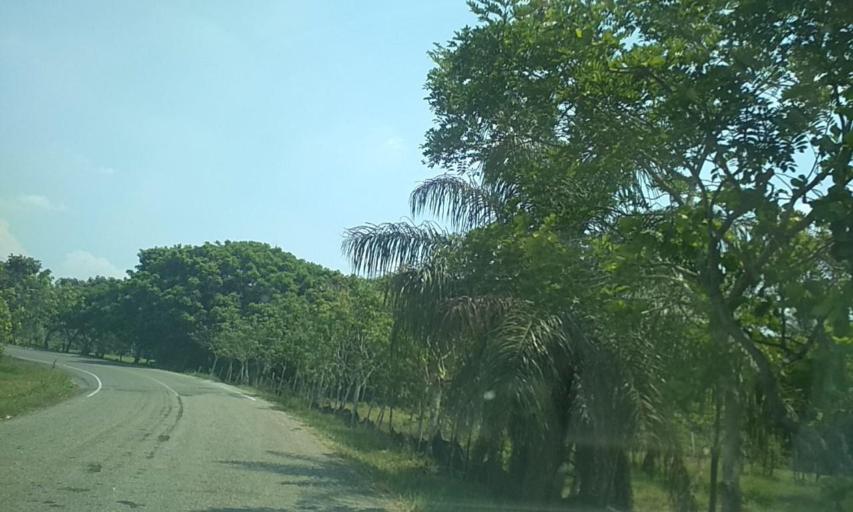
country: MX
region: Tabasco
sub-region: Huimanguillo
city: C-41 (Licenciado Carlos A. Madrazo)
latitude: 17.8305
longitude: -93.5131
